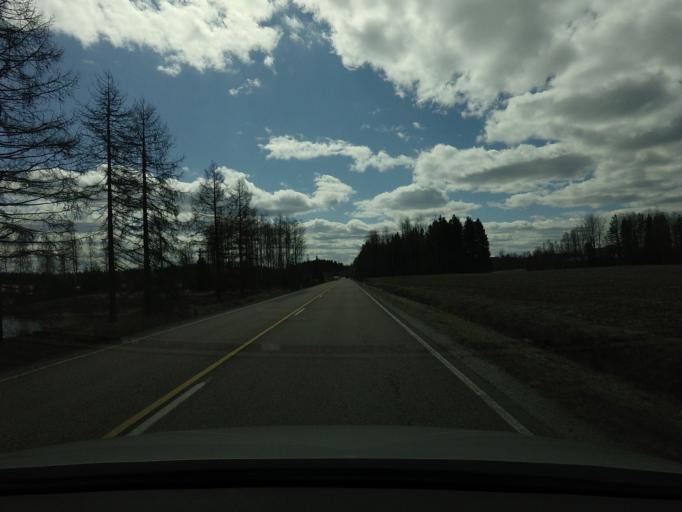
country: FI
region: South Karelia
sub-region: Lappeenranta
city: Taavetti
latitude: 60.9163
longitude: 27.5758
